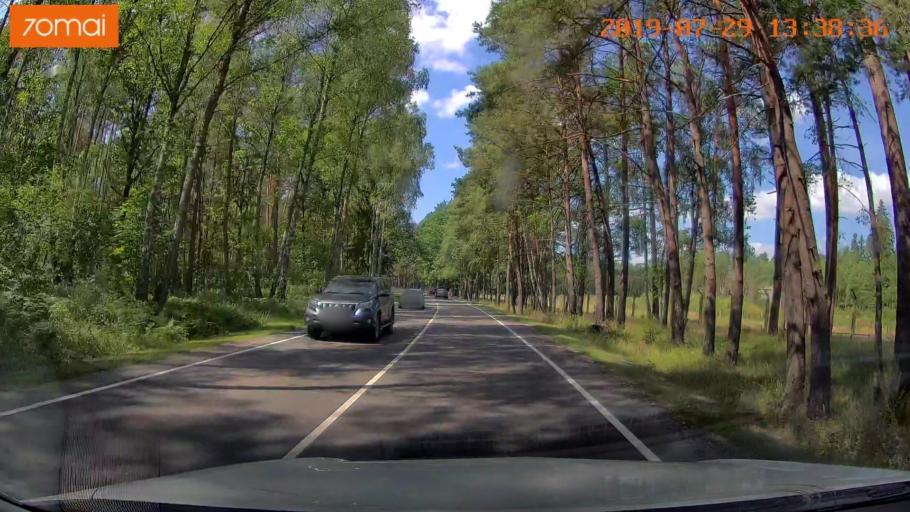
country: RU
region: Kaliningrad
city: Volochayevskoye
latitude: 54.7220
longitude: 20.1685
